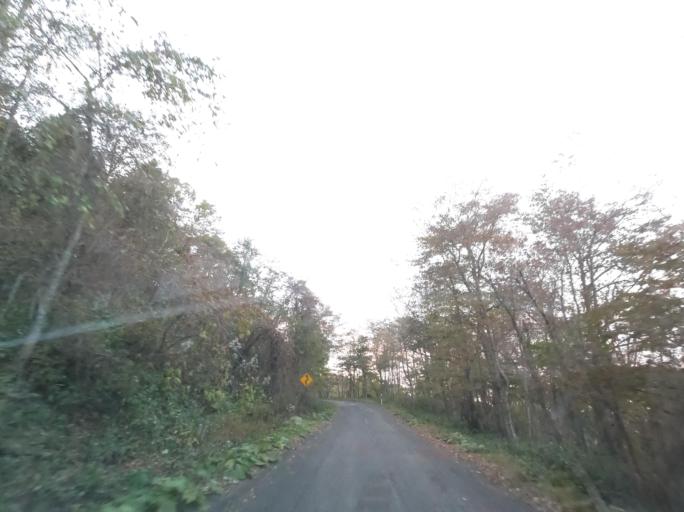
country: JP
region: Hokkaido
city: Kushiro
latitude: 43.1992
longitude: 144.4596
